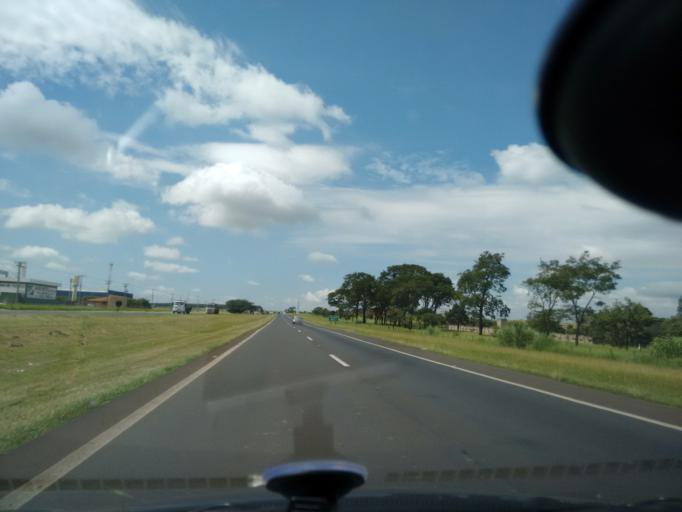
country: BR
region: Sao Paulo
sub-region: Ibate
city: Ibate
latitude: -21.9370
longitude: -48.0118
